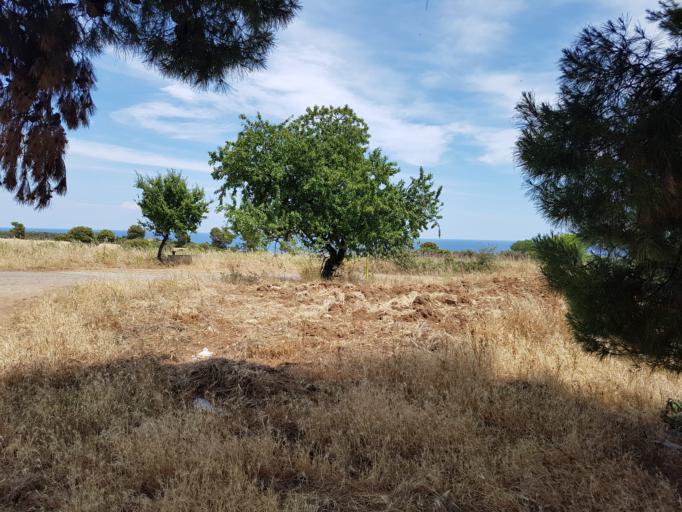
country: IT
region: Calabria
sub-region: Provincia di Cosenza
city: Amendolara
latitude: 39.9267
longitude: 16.5786
